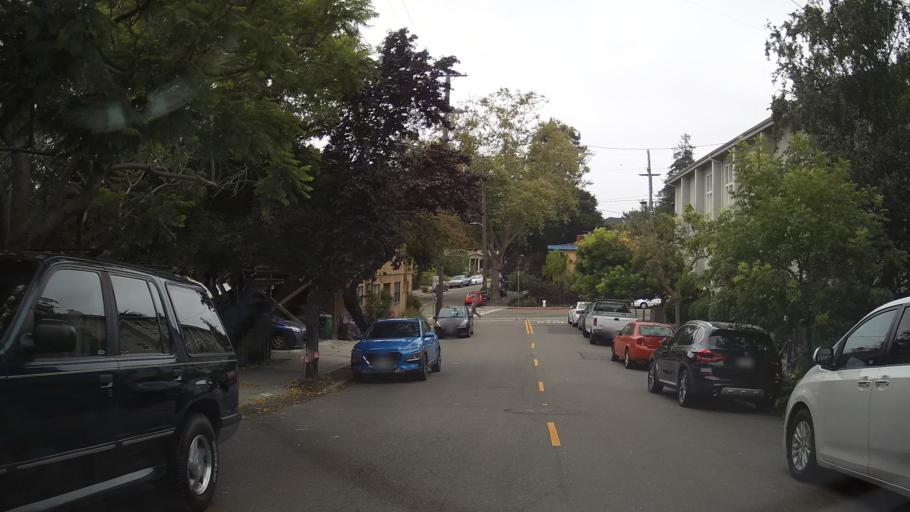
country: US
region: California
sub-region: Alameda County
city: Berkeley
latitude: 37.8820
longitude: -122.2798
